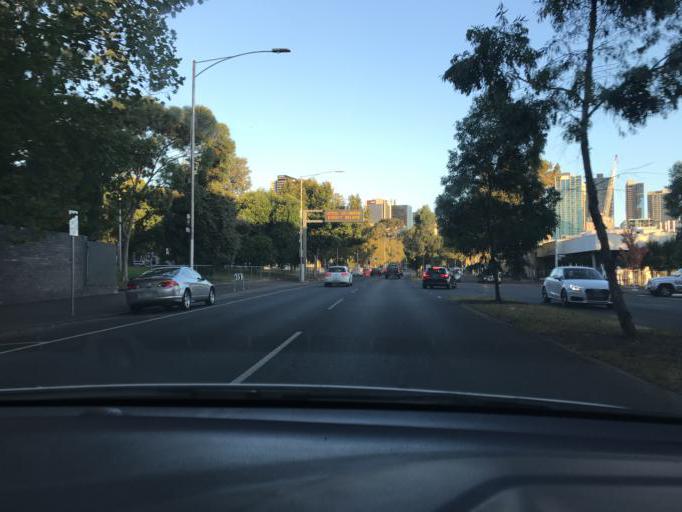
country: AU
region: Victoria
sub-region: Melbourne
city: West Melbourne
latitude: -37.8067
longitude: 144.9504
